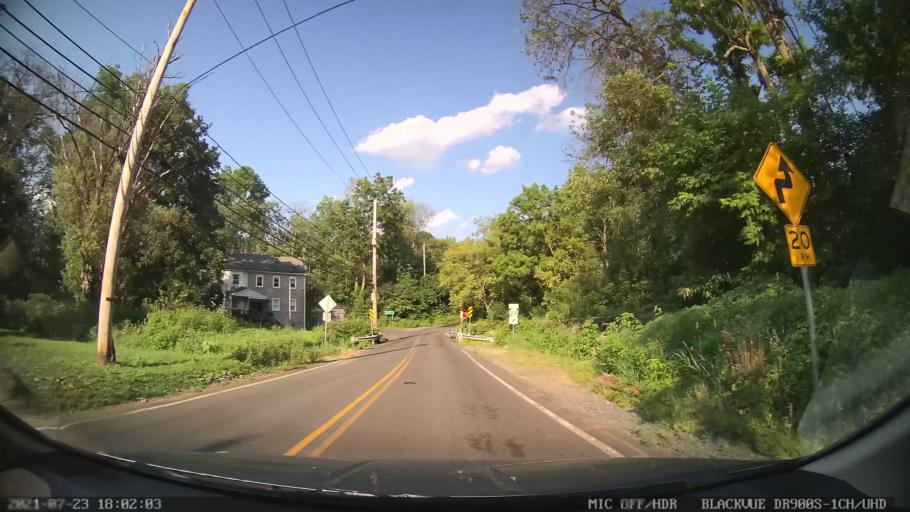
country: US
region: Pennsylvania
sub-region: Lehigh County
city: Emmaus
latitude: 40.5340
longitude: -75.5154
